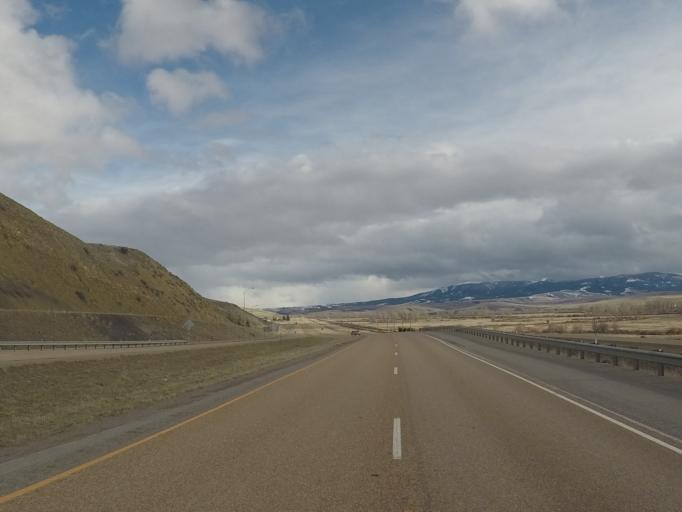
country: US
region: Montana
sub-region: Granite County
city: Philipsburg
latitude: 46.6642
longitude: -113.1377
